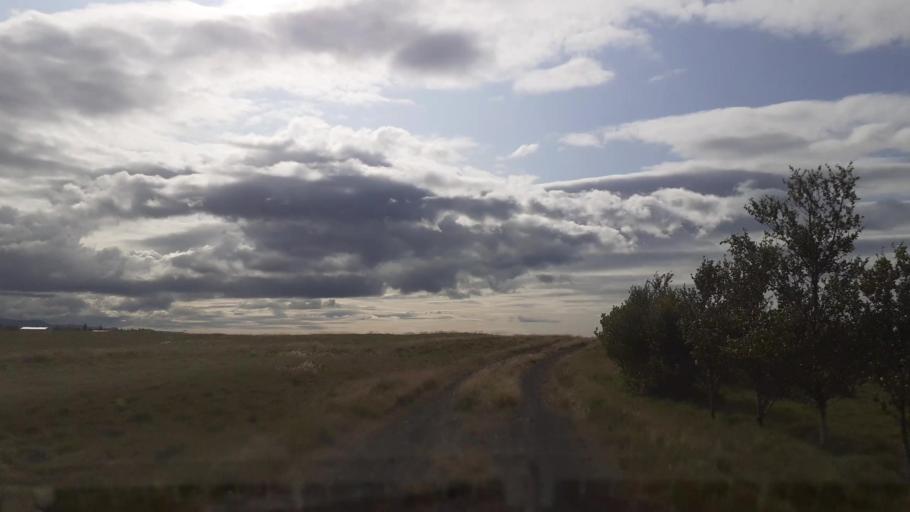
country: IS
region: South
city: Vestmannaeyjar
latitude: 63.7742
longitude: -20.2992
